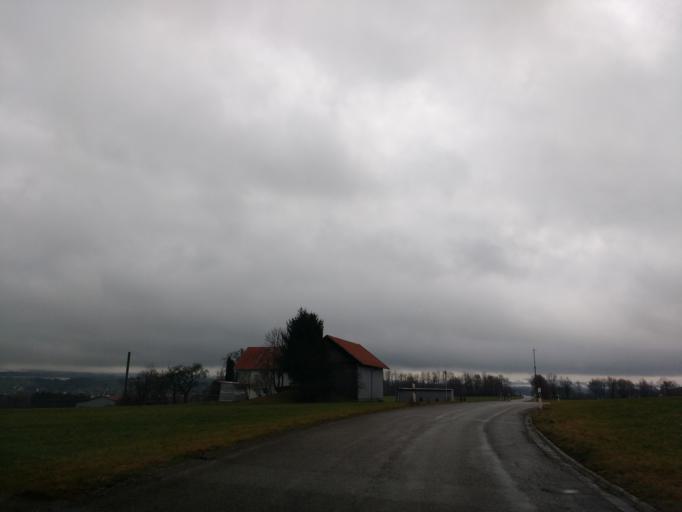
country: DE
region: Bavaria
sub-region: Swabia
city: Neuburg
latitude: 47.7461
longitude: 10.3508
